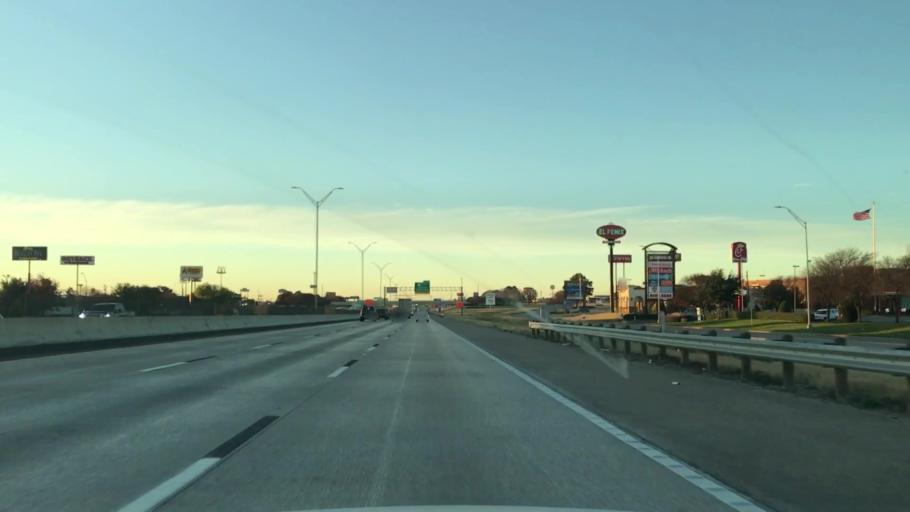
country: US
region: Texas
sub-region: Johnson County
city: Burleson
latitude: 32.5681
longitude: -97.3190
